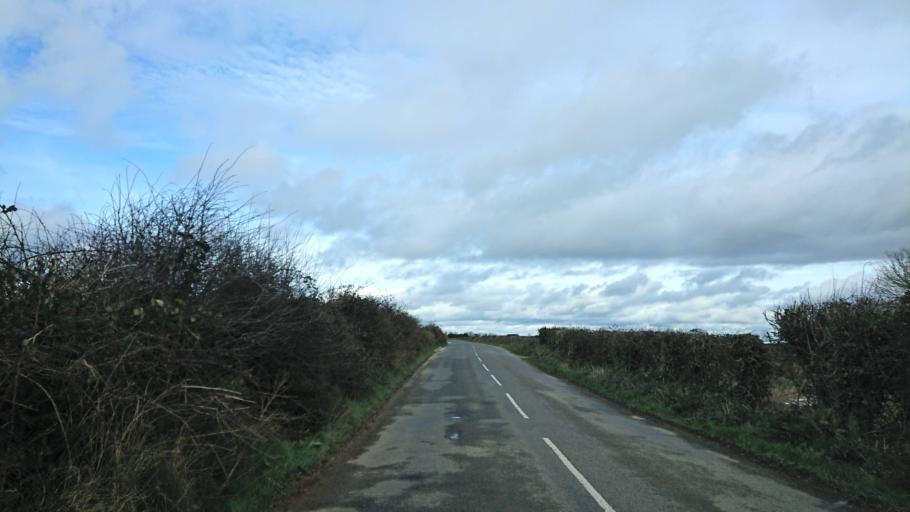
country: IE
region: Munster
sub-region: Waterford
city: Dunmore East
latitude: 52.2427
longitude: -6.9078
